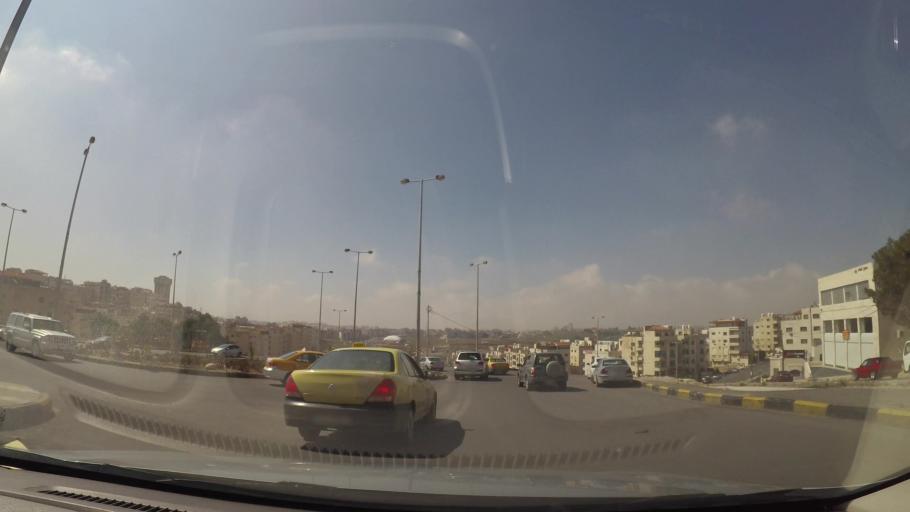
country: JO
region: Amman
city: Al Bunayyat ash Shamaliyah
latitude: 31.9147
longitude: 35.8873
